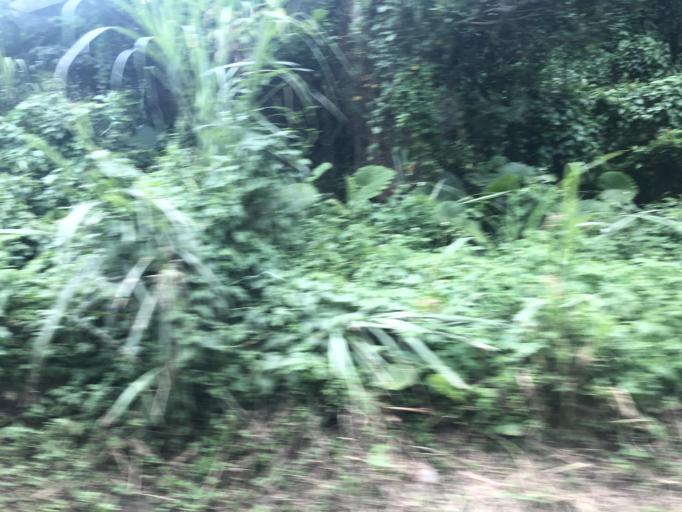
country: TW
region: Taiwan
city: Daxi
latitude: 24.9123
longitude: 121.3408
